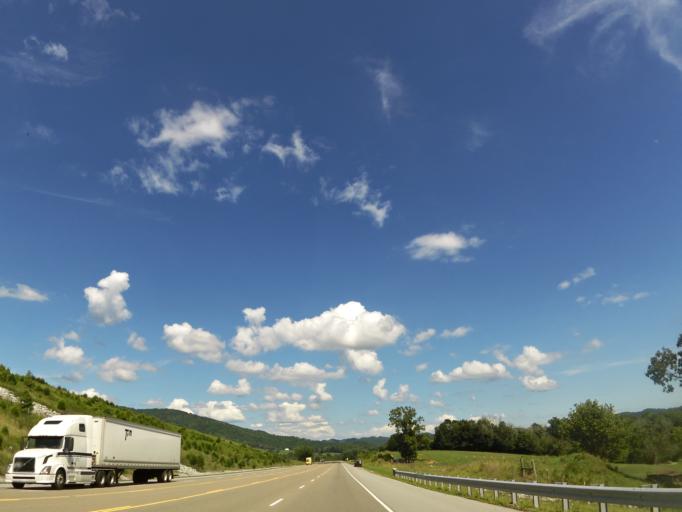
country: US
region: Tennessee
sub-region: Claiborne County
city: Tazewell
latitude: 36.4216
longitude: -83.5444
